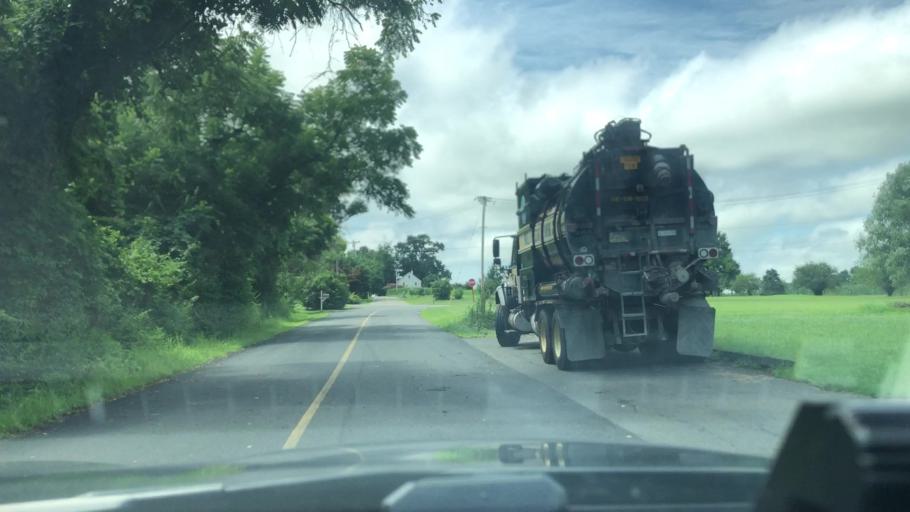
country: US
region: Pennsylvania
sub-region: Chester County
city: Spring City
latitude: 40.1932
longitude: -75.5767
